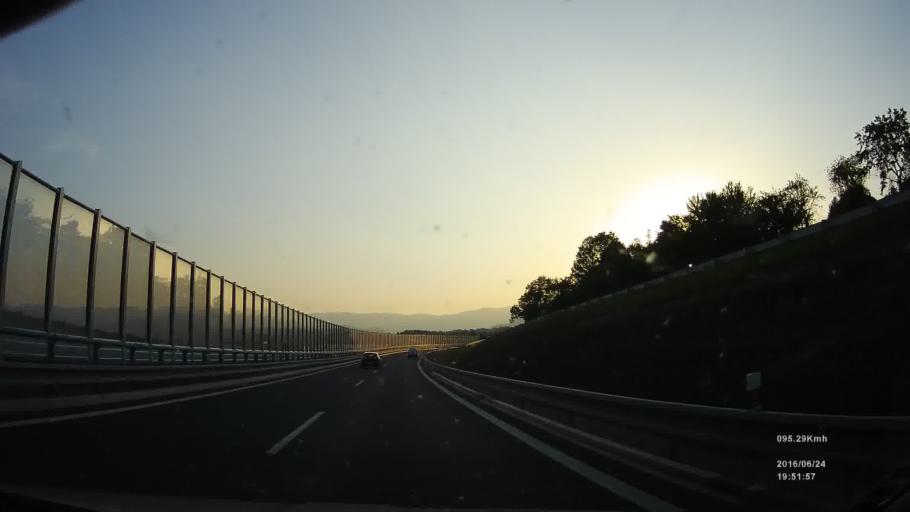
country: SK
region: Banskobystricky
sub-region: Okres Banska Bystrica
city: Banska Bystrica
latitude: 48.7433
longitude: 19.1619
